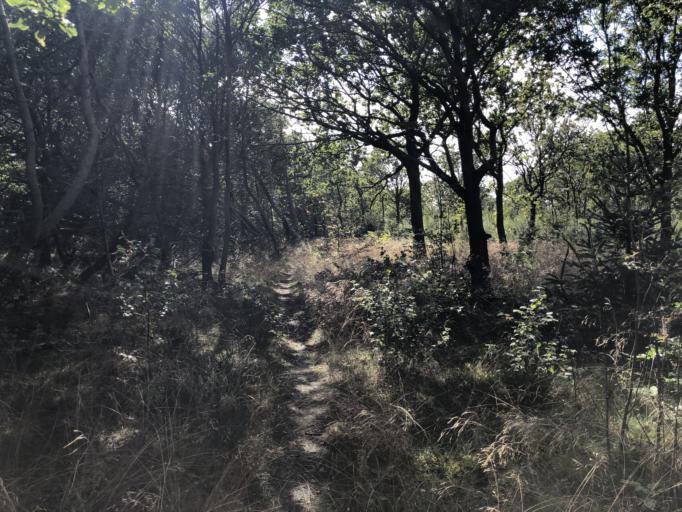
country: DK
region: Central Jutland
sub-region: Holstebro Kommune
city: Ulfborg
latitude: 56.3858
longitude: 8.3618
